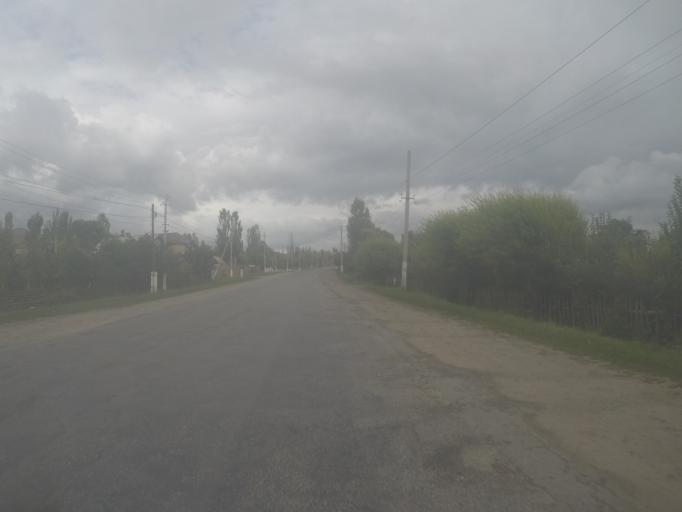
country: KG
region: Ysyk-Koel
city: Tyup
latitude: 42.7474
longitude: 78.0895
